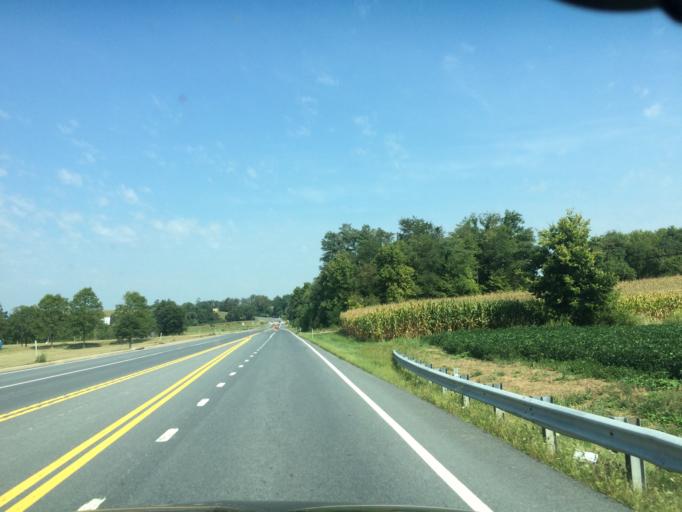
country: US
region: Maryland
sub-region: Carroll County
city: New Windsor
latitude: 39.5490
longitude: -77.1110
